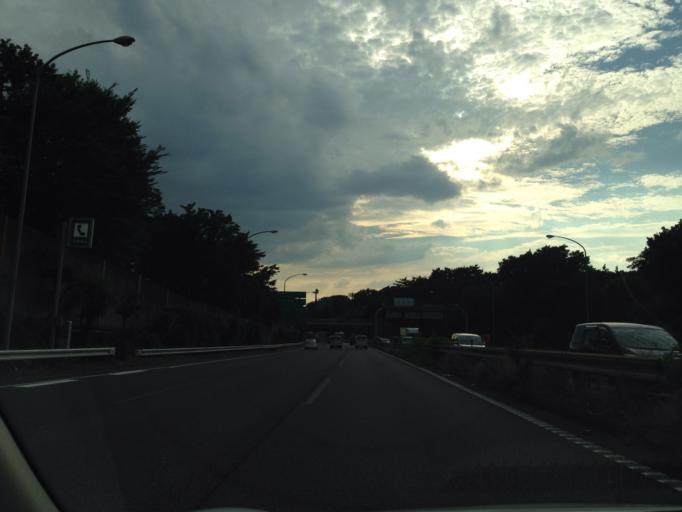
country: JP
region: Tokyo
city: Chofugaoka
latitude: 35.6283
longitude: 139.6177
